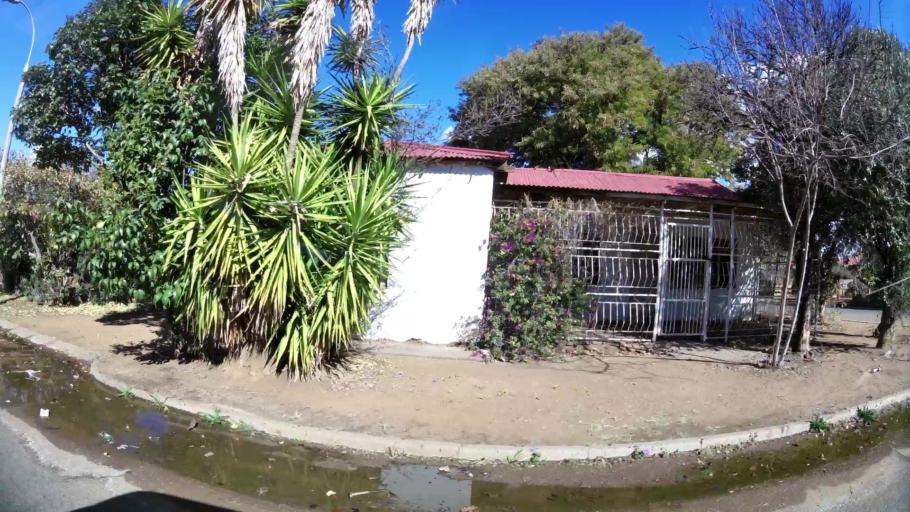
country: ZA
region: North-West
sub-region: Dr Kenneth Kaunda District Municipality
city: Klerksdorp
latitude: -26.8625
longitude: 26.6459
